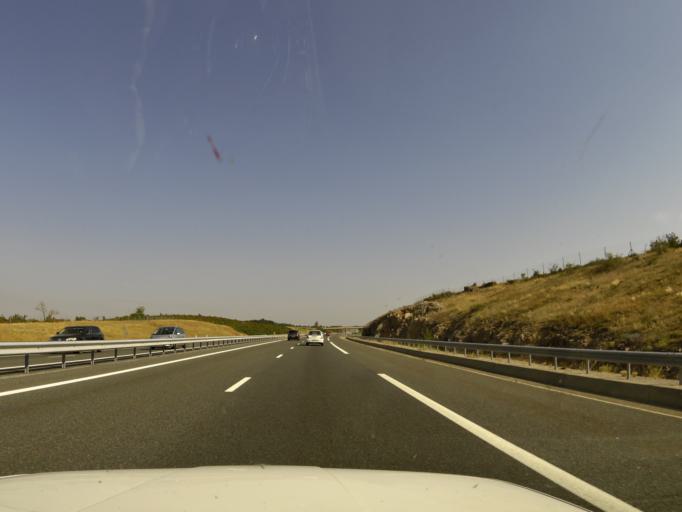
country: FR
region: Midi-Pyrenees
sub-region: Departement de l'Aveyron
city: Creissels
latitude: 44.0485
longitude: 3.0518
